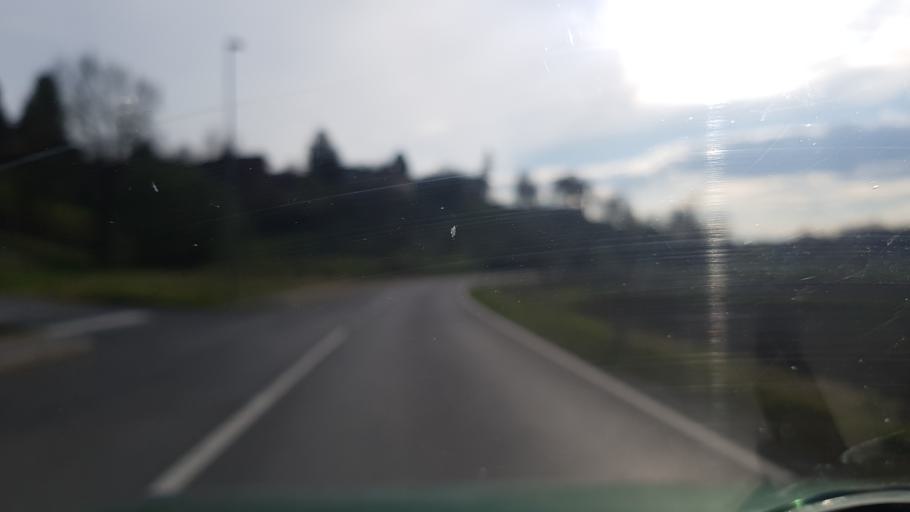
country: SI
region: Nova Gorica
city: Prvacina
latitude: 45.9080
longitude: 13.7032
